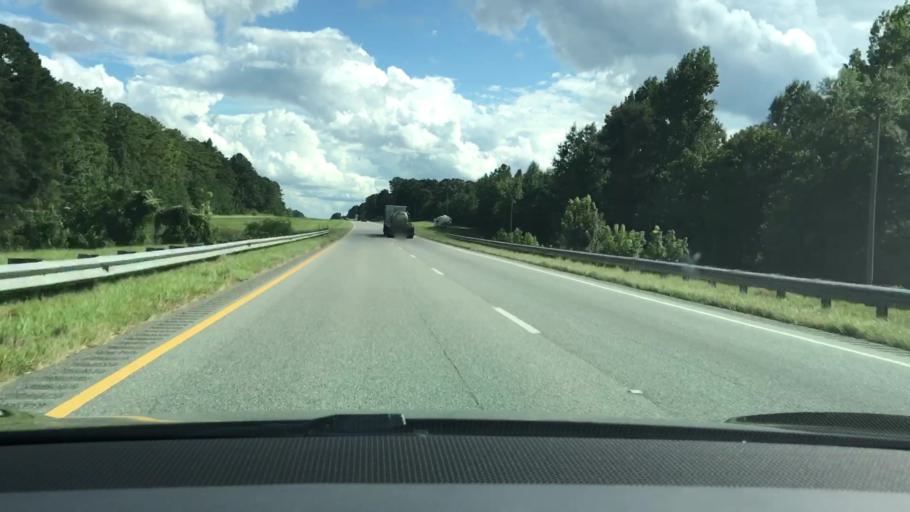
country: US
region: Alabama
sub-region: Montgomery County
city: Taylor
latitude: 32.0254
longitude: -86.0321
